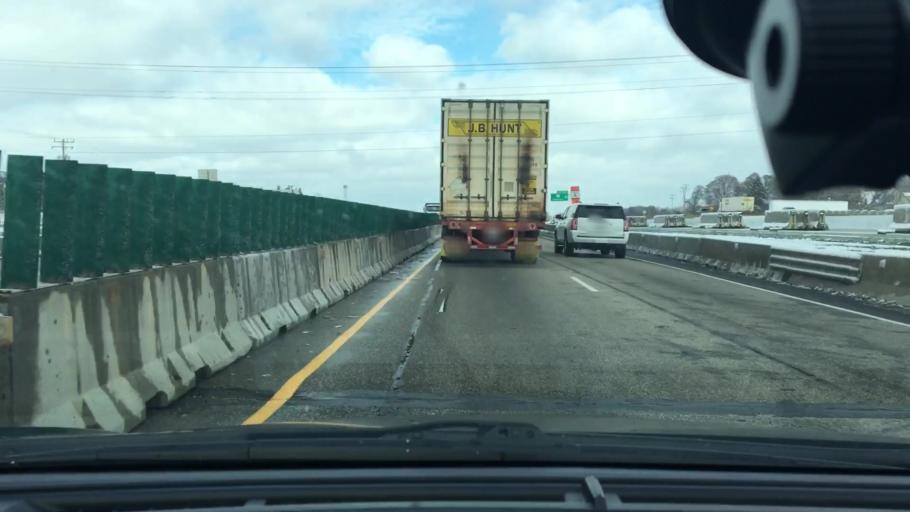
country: US
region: Wisconsin
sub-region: Racine County
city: Caledonia
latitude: 42.7997
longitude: -87.9531
